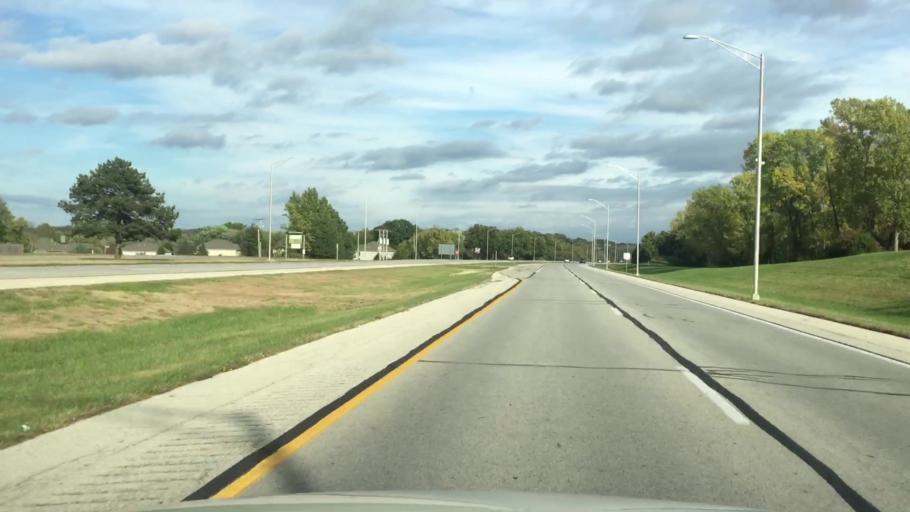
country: US
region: Kansas
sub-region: Wyandotte County
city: Edwardsville
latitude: 39.0087
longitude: -94.8345
